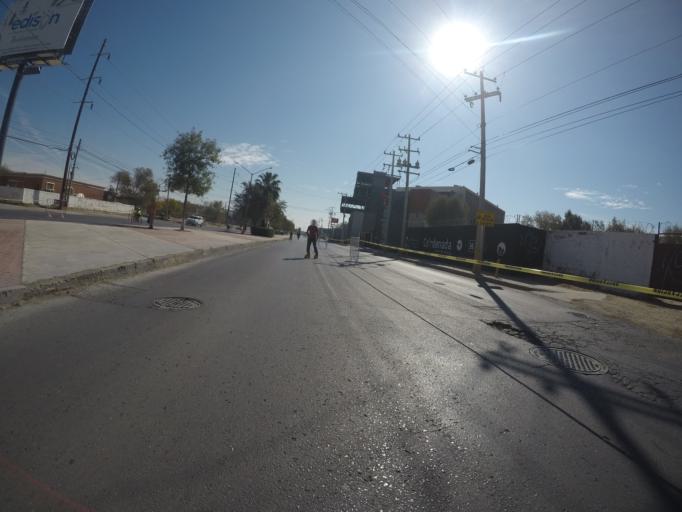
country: MX
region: Chihuahua
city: Ciudad Juarez
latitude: 31.7267
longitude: -106.4050
